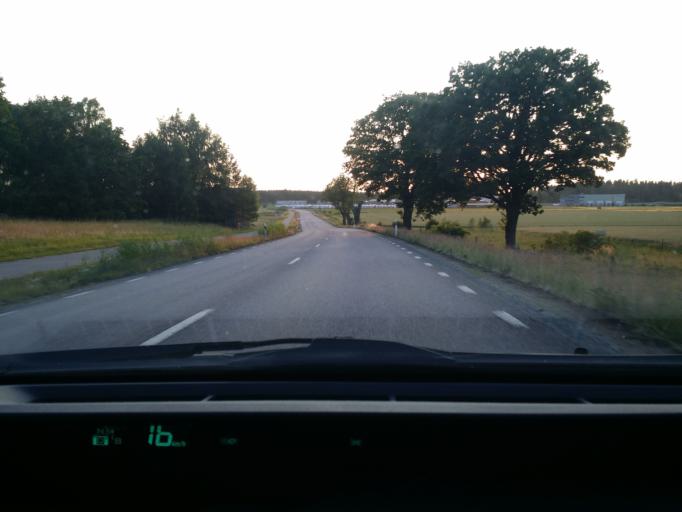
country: SE
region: Vaestmanland
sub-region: Vasteras
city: Tillberga
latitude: 59.6062
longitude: 16.6482
